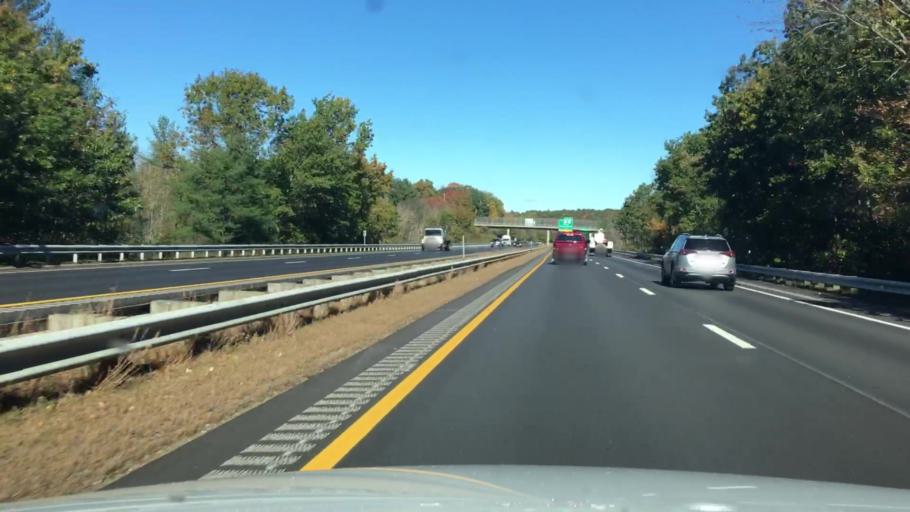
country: US
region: New Hampshire
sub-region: Strafford County
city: Dover
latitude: 43.1974
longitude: -70.8957
